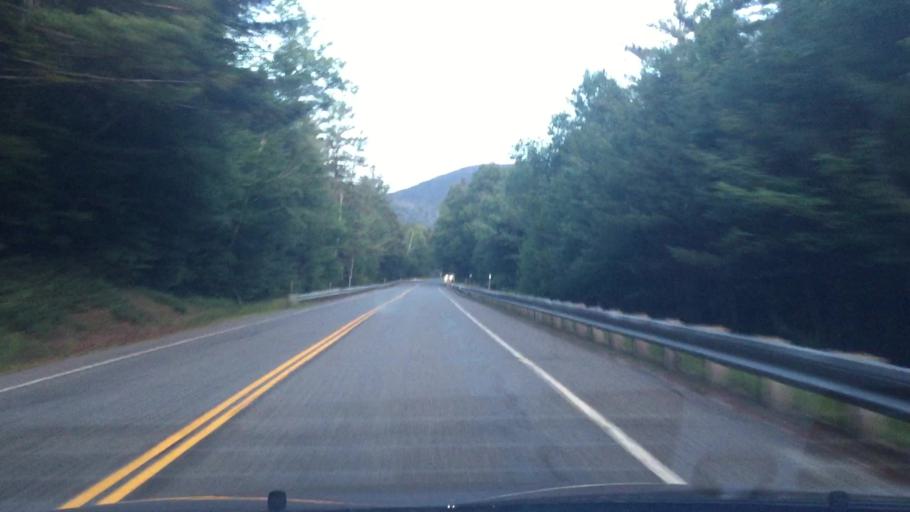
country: US
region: New Hampshire
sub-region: Grafton County
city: Woodstock
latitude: 44.0362
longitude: -71.5306
